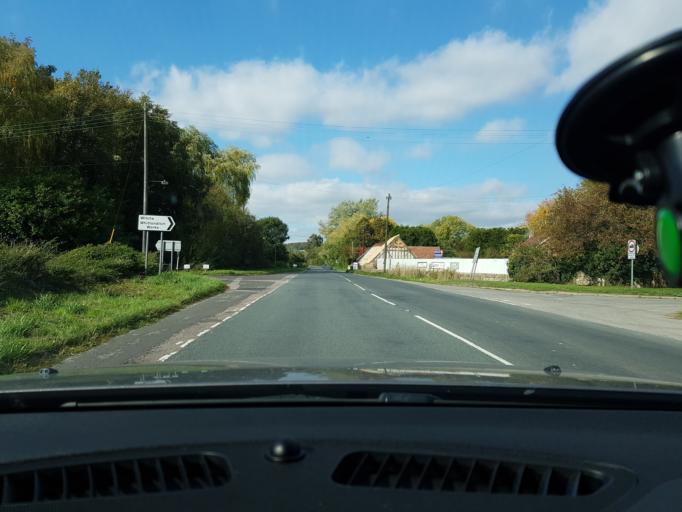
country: GB
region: England
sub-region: Wiltshire
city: Ramsbury
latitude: 51.4493
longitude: -1.5851
